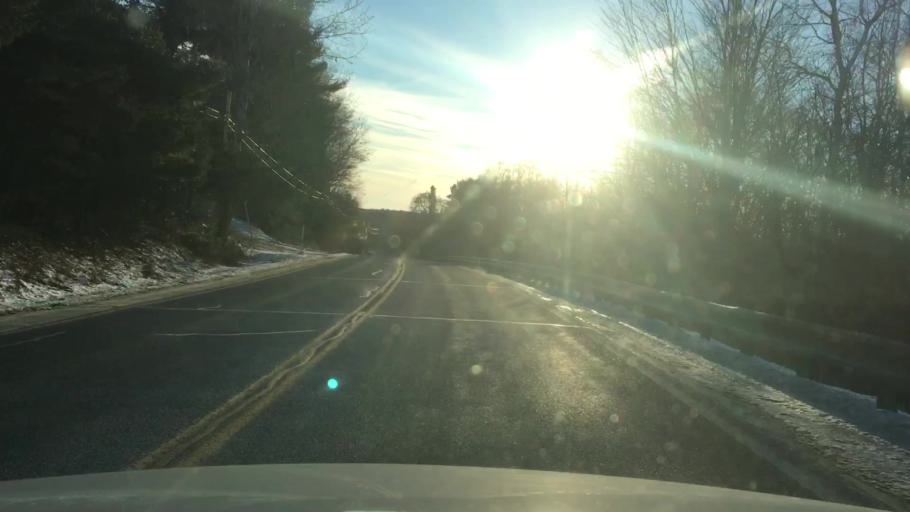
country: US
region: Maine
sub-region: Penobscot County
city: Eddington
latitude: 44.8265
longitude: -68.6906
